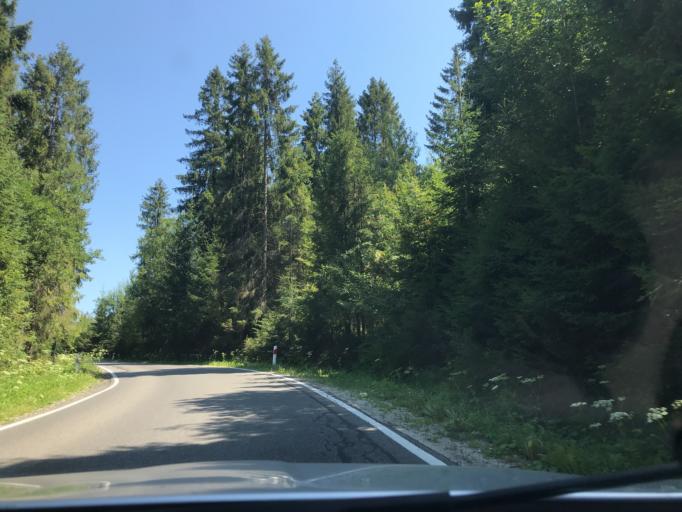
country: PL
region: Lesser Poland Voivodeship
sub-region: Powiat nowotarski
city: Klikuszowa
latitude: 49.5251
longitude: 19.9637
